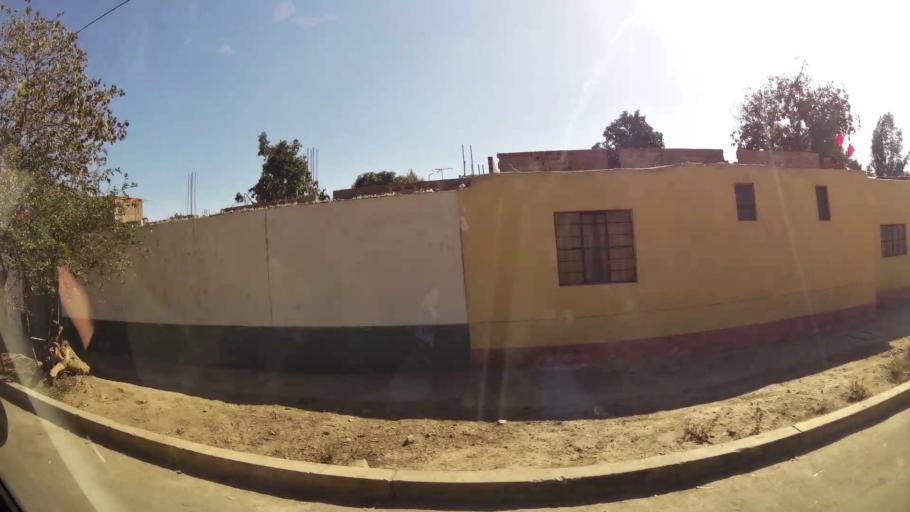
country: PE
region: Ica
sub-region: Provincia de Ica
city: La Tinguina
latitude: -14.0369
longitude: -75.7125
